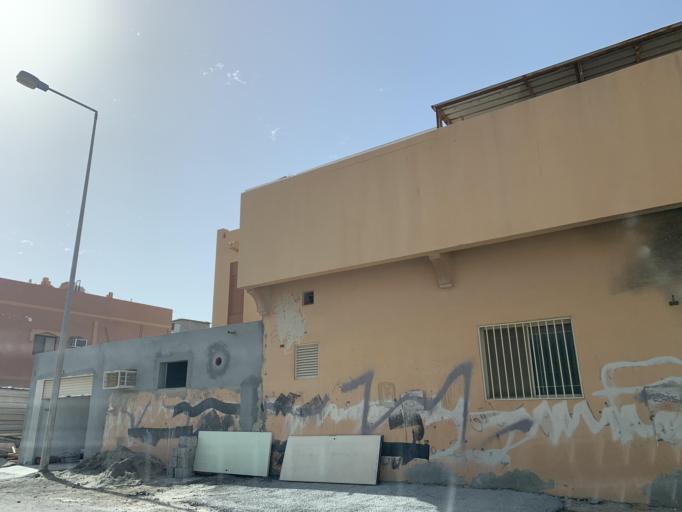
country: BH
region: Northern
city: Sitrah
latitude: 26.1463
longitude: 50.6112
